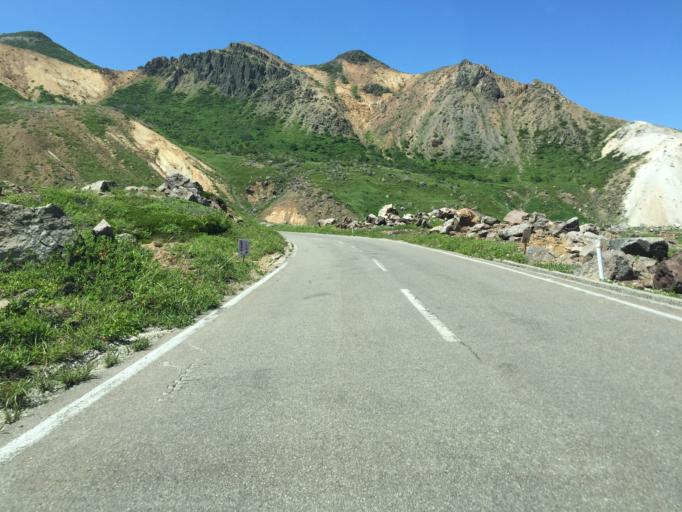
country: JP
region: Fukushima
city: Fukushima-shi
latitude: 37.7294
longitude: 140.2593
